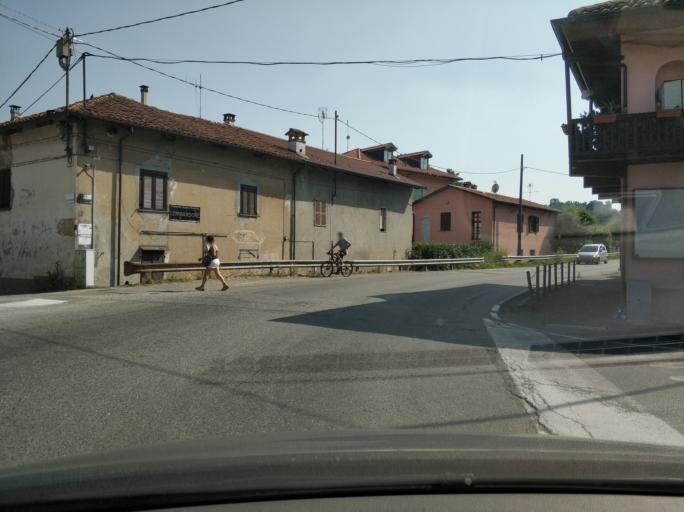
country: IT
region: Piedmont
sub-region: Provincia di Torino
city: Lombardore
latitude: 45.2352
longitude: 7.7414
